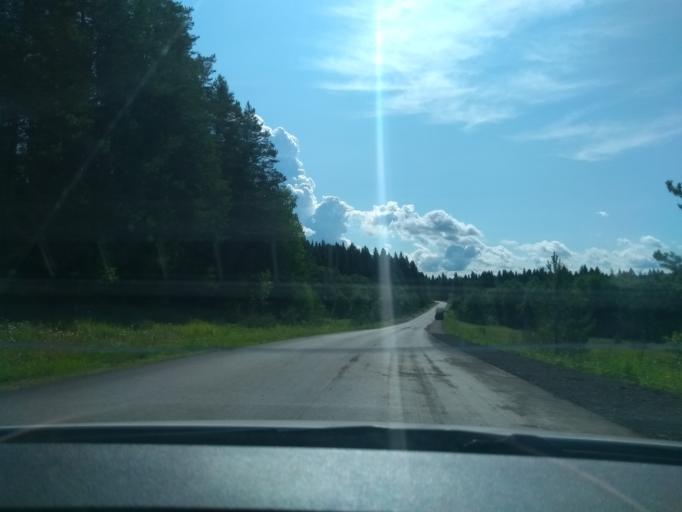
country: RU
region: Perm
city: Bershet'
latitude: 57.8202
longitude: 56.5236
